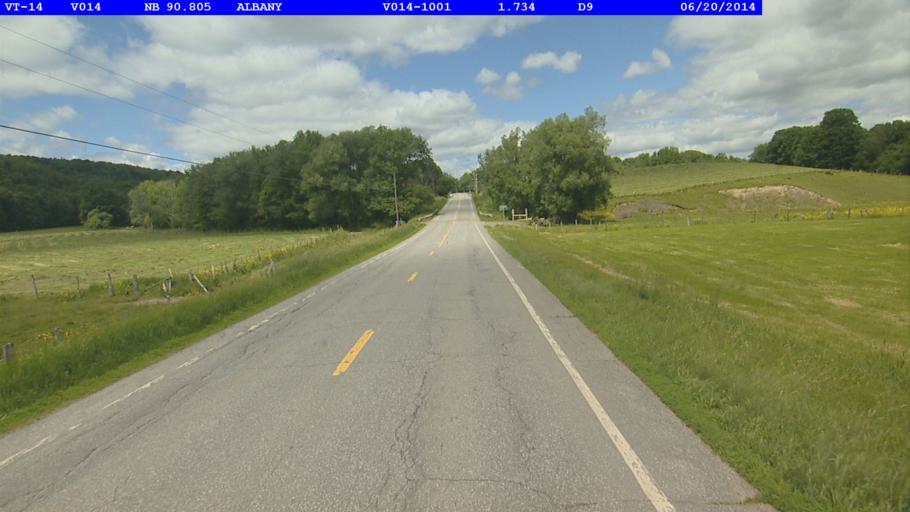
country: US
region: Vermont
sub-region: Caledonia County
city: Hardwick
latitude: 44.7263
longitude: -72.3821
